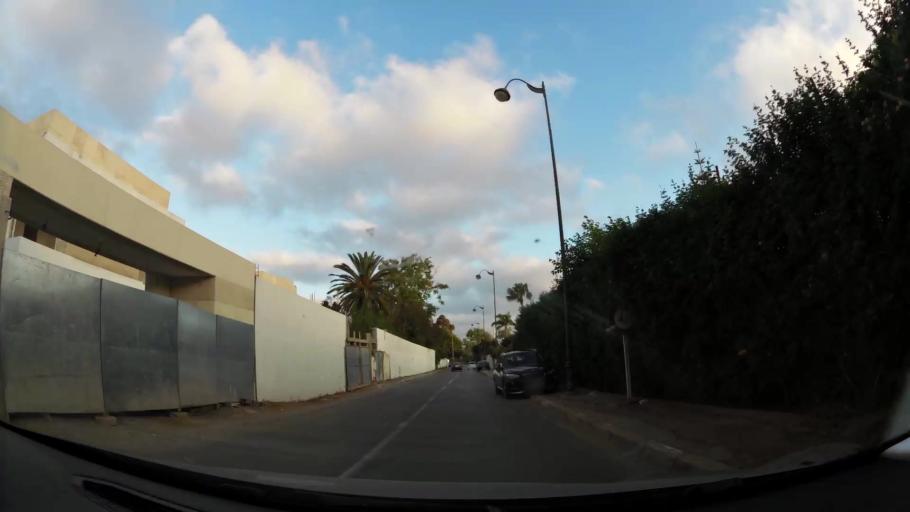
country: MA
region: Rabat-Sale-Zemmour-Zaer
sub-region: Rabat
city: Rabat
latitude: 33.9724
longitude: -6.8409
